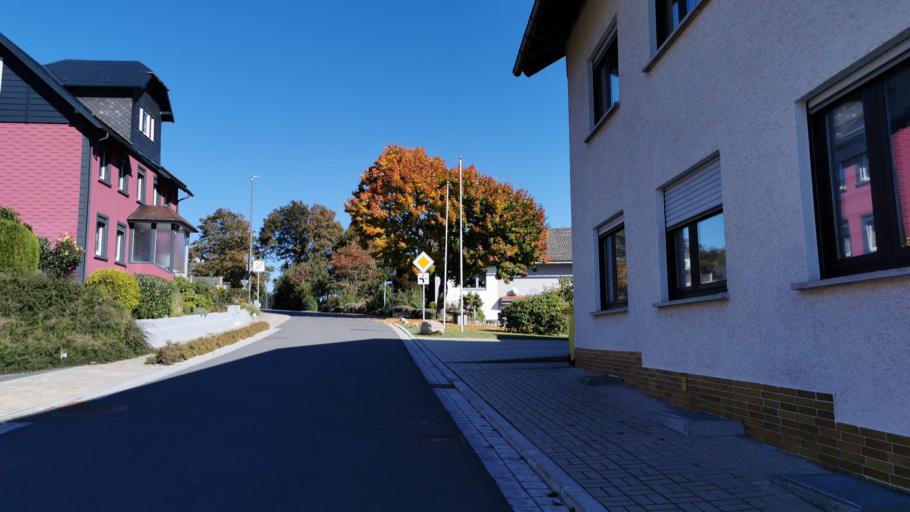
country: DE
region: Bavaria
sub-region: Upper Franconia
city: Tettau
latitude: 50.4748
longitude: 11.2899
